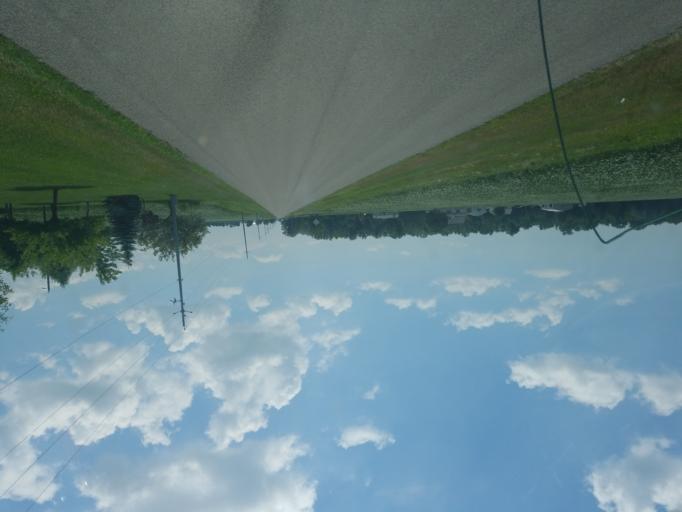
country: US
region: Ohio
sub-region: Mercer County
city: Celina
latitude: 40.5955
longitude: -84.4940
